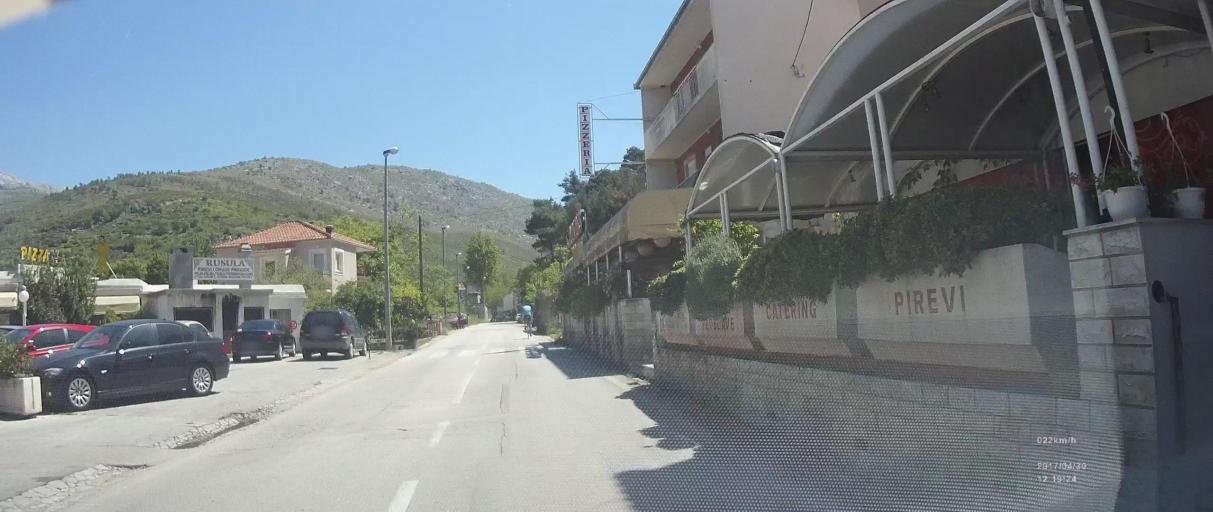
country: HR
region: Splitsko-Dalmatinska
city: Zrnovnica
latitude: 43.5167
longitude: 16.5542
